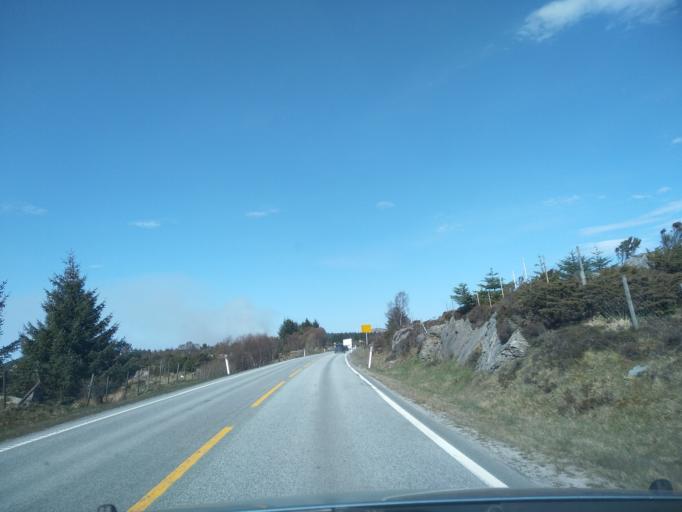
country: NO
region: Rogaland
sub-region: Tysvaer
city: Tysvaer
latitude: 59.3115
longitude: 5.4733
